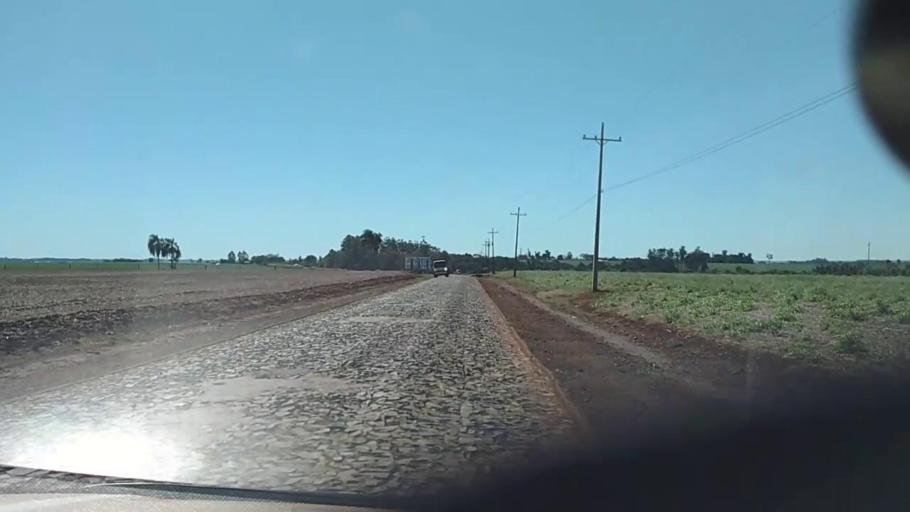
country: PY
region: Alto Parana
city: Naranjal
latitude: -25.9678
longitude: -55.1479
